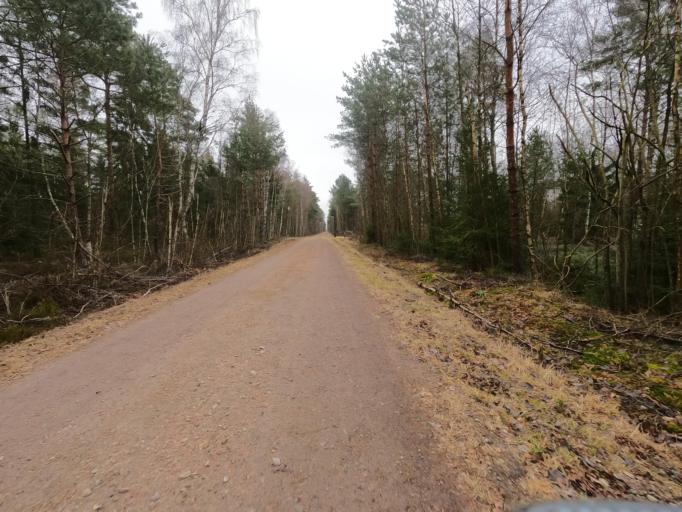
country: SE
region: Kronoberg
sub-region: Ljungby Kommun
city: Ljungby
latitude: 56.8214
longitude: 13.7137
